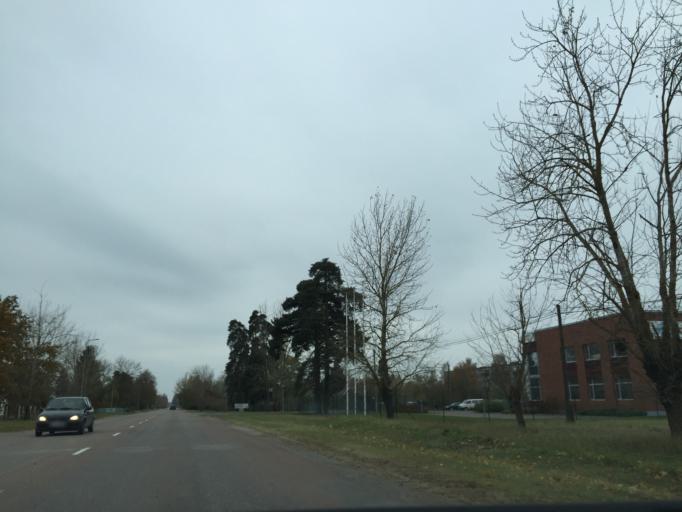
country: LV
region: Marupe
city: Marupe
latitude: 56.8862
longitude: 24.0707
